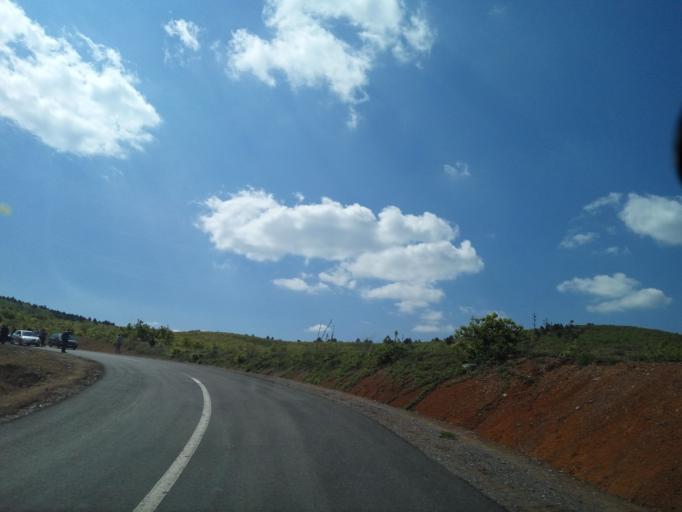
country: XK
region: Gjakova
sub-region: Komuna e Gjakoves
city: Gjakove
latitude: 42.3145
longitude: 20.4480
